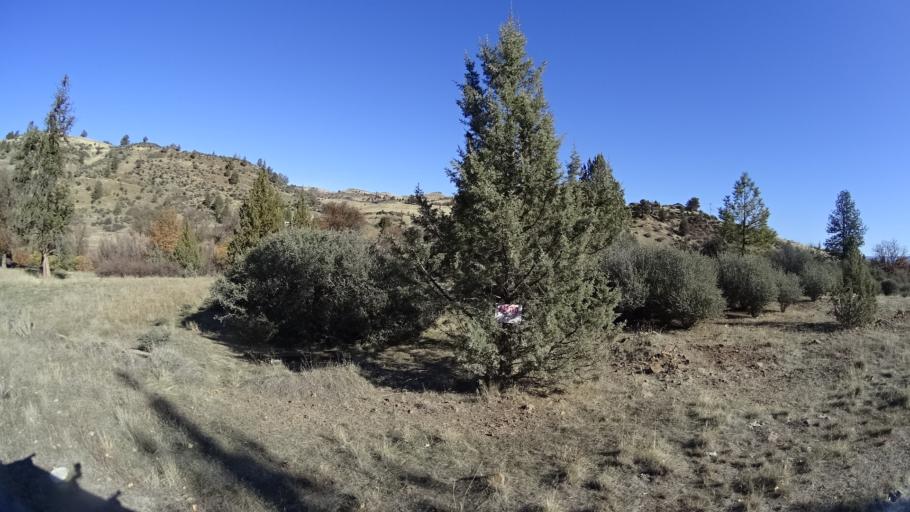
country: US
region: California
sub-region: Siskiyou County
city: Montague
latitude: 41.8986
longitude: -122.5104
